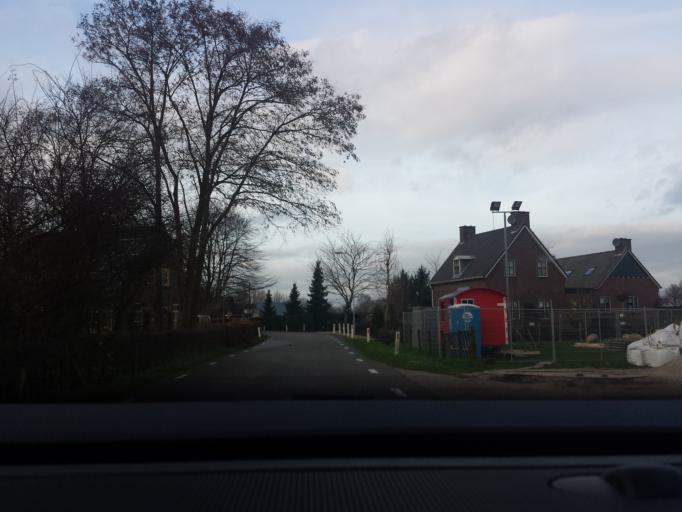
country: NL
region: Gelderland
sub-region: Gemeente Zevenaar
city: Zevenaar
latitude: 51.9270
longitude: 6.1471
